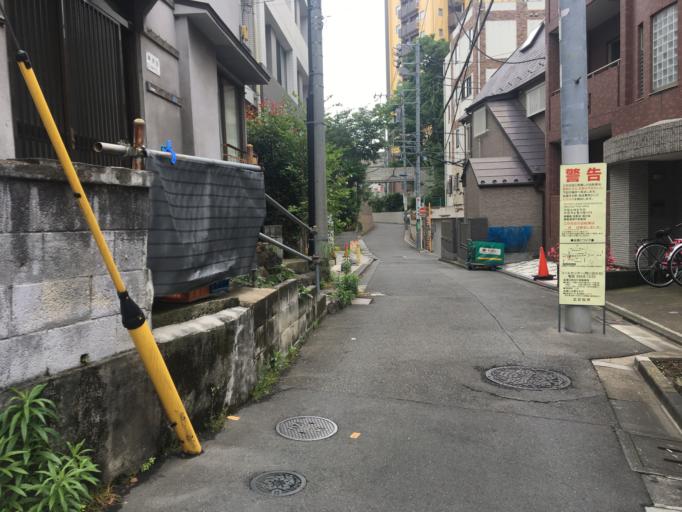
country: JP
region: Saitama
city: Kawaguchi
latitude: 35.7786
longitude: 139.7182
